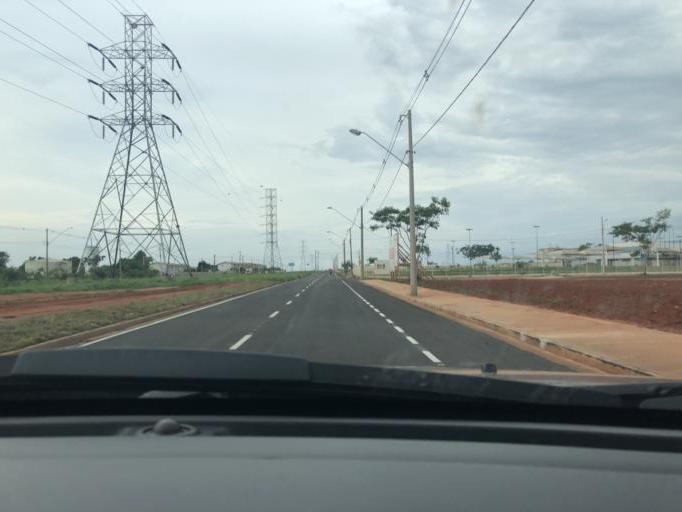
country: BR
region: Sao Paulo
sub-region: Sao Jose Do Rio Preto
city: Sao Jose do Rio Preto
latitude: -20.8370
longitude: -49.4216
